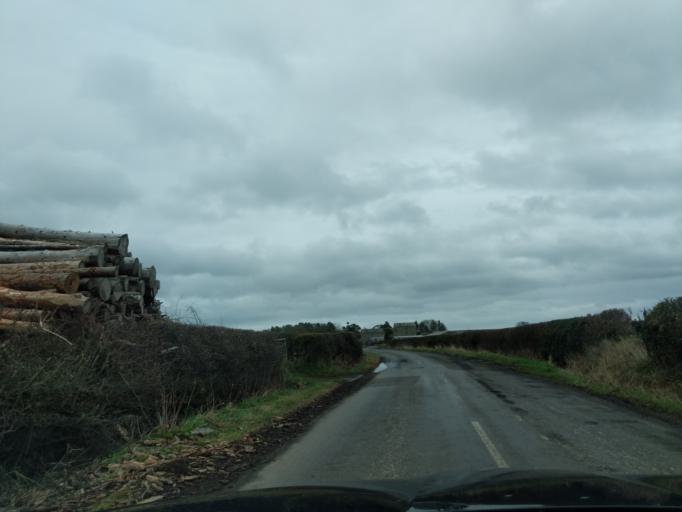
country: GB
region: England
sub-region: Northumberland
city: Morpeth
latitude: 55.1803
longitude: -1.7300
